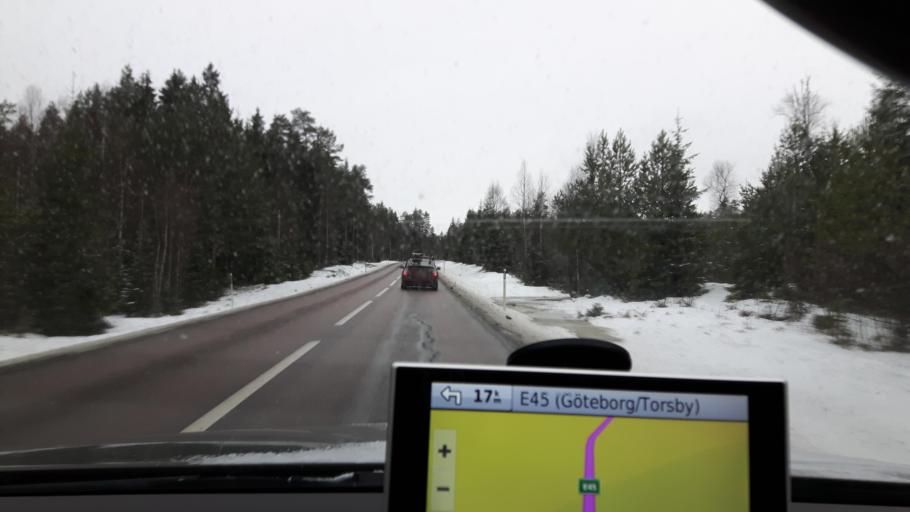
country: SE
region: Vaermland
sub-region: Hagfors Kommun
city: Ekshaerad
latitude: 60.3838
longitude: 13.2437
